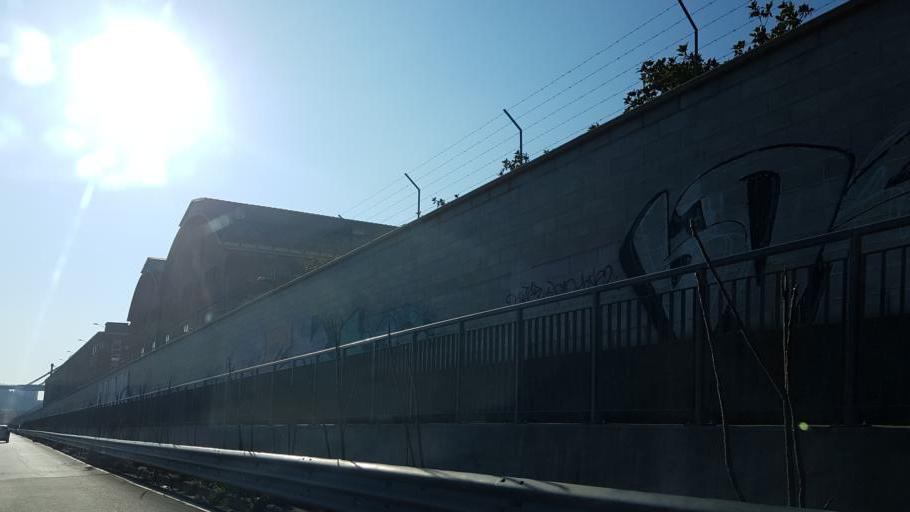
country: IT
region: Liguria
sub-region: Provincia di Genova
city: Genoa
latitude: 44.4338
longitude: 8.8895
